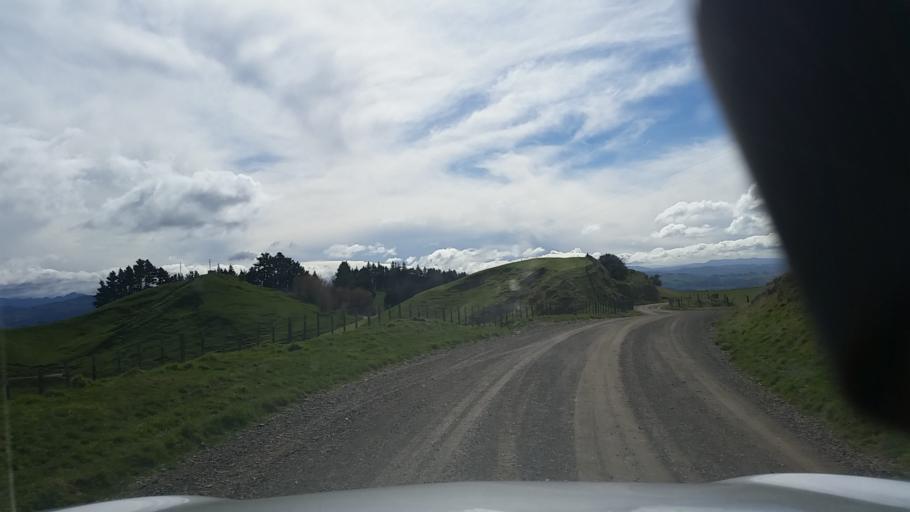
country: NZ
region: Hawke's Bay
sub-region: Napier City
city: Napier
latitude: -39.2022
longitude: 176.9511
